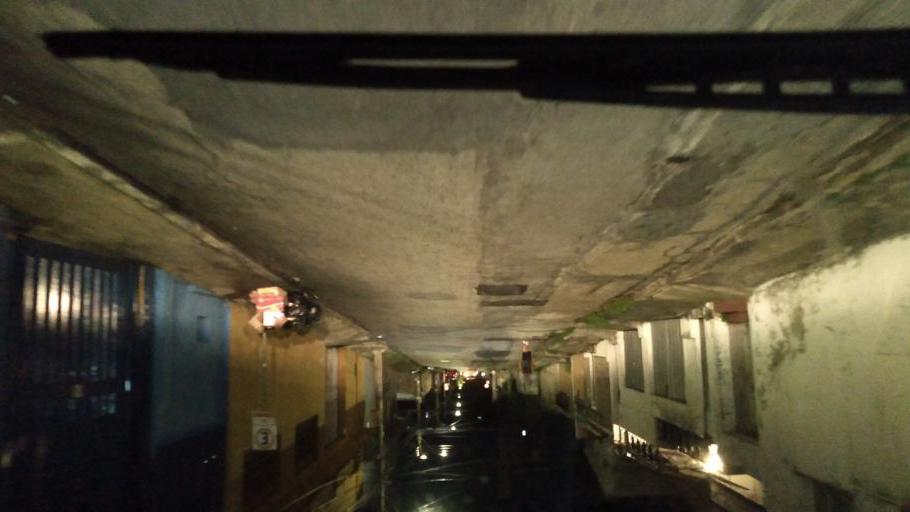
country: BR
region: Minas Gerais
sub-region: Belo Horizonte
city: Belo Horizonte
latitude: -19.9108
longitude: -43.9580
